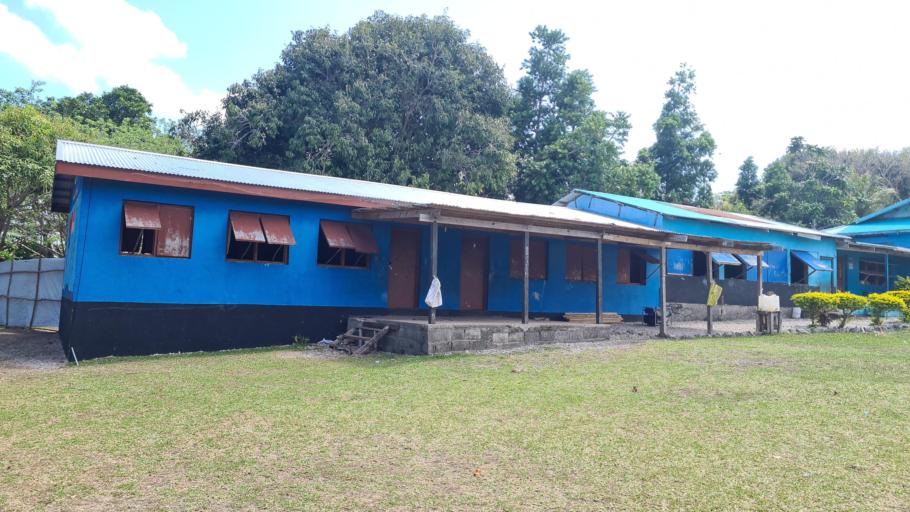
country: VU
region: Shefa
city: Port-Vila
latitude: -17.4824
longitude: 168.3868
